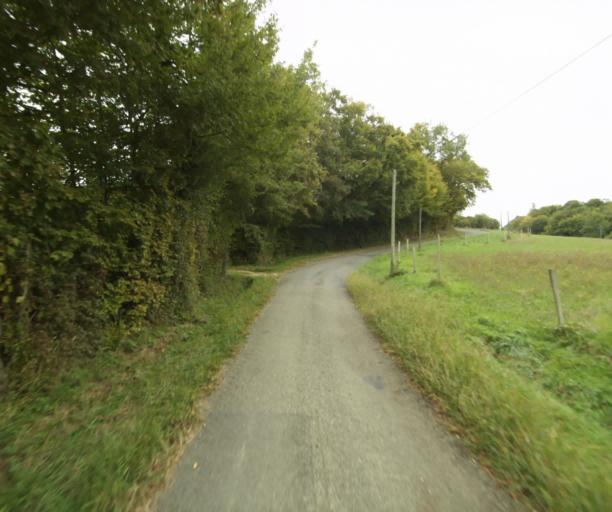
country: FR
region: Midi-Pyrenees
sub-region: Departement du Gers
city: Eauze
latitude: 43.8966
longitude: 0.0593
